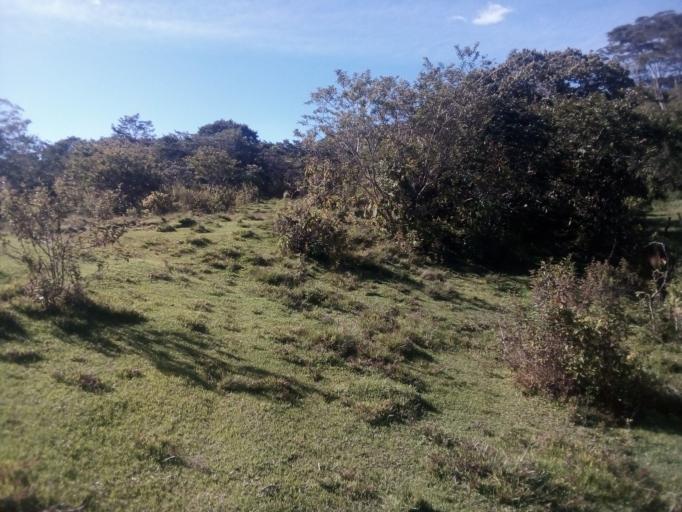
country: CO
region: Santander
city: Guepsa
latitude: 5.9910
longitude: -73.5537
